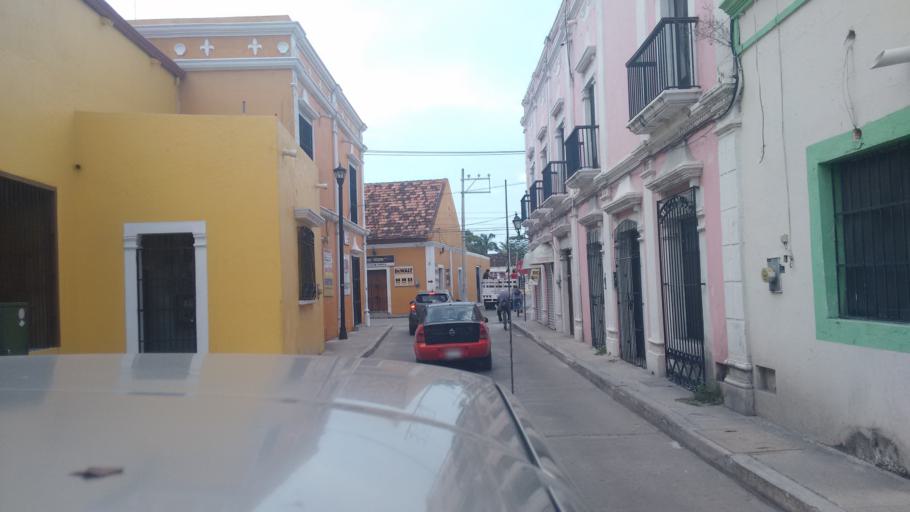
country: MX
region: Campeche
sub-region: Carmen
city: Ciudad del Carmen
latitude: 18.6351
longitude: -91.8331
